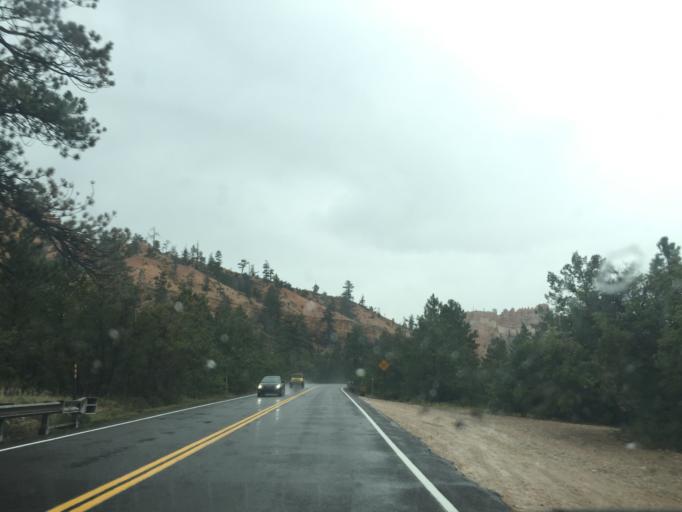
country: US
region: Utah
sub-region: Garfield County
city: Panguitch
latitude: 37.6628
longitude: -112.1070
